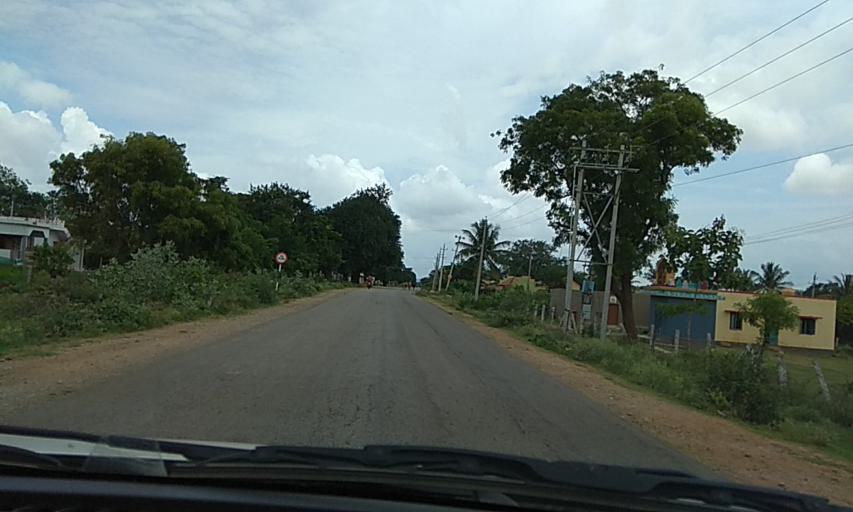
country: IN
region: Karnataka
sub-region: Chamrajnagar
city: Gundlupet
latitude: 11.8109
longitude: 76.7387
